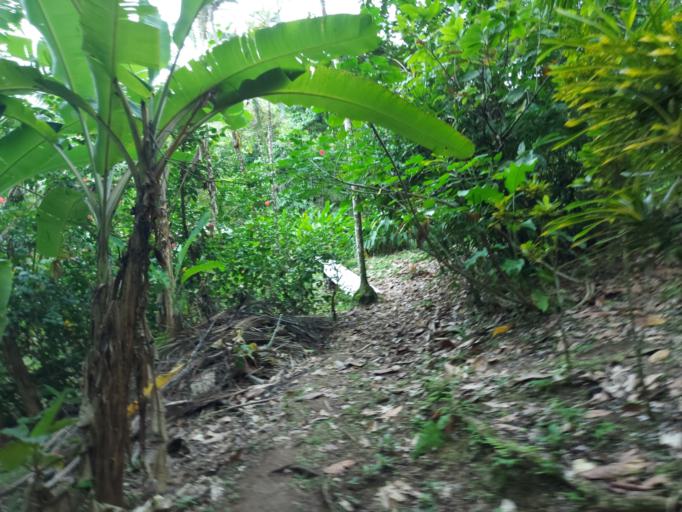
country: PA
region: Bocas del Toro
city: Barranco
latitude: 9.6411
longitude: -82.7839
